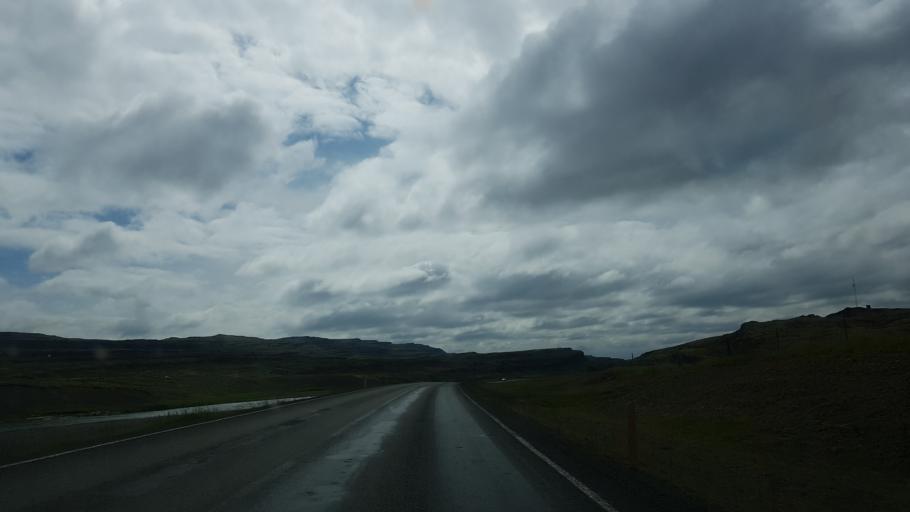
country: IS
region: West
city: Borgarnes
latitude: 64.8107
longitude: -21.4164
